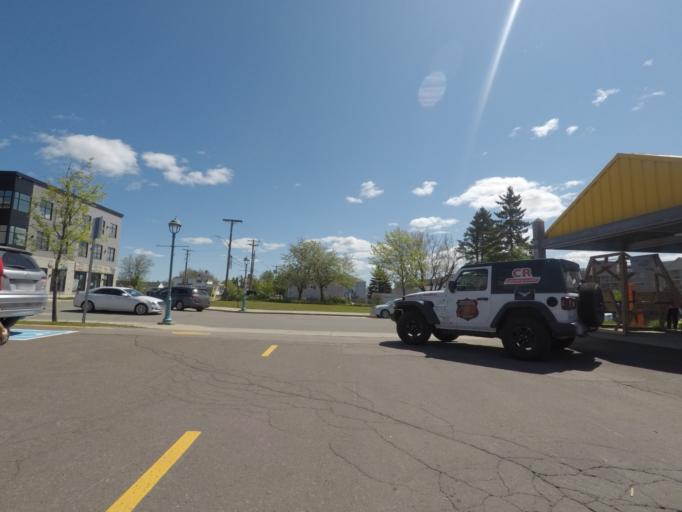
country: CA
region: New Brunswick
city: Moncton
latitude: 46.0944
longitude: -64.7461
